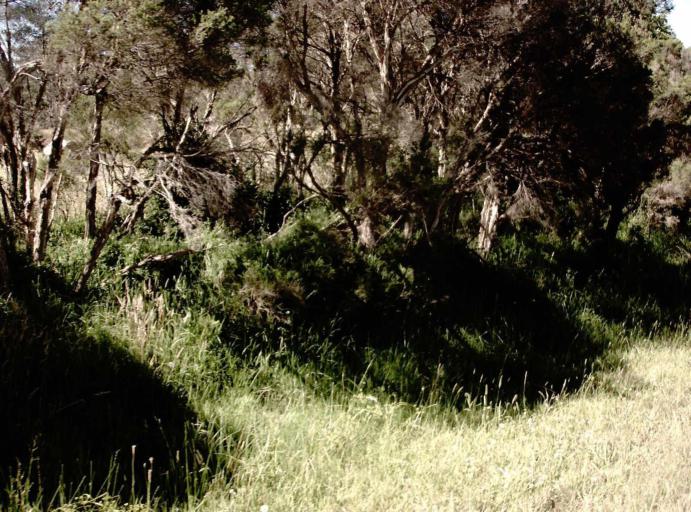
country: AU
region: Victoria
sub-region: Latrobe
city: Morwell
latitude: -38.6448
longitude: 146.4793
